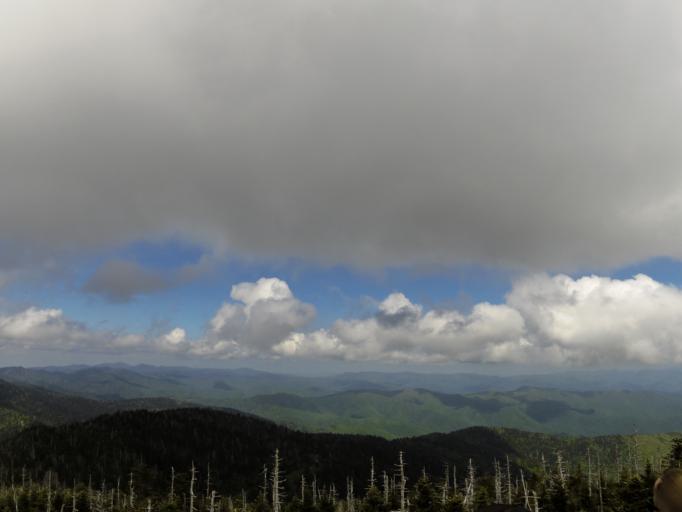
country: US
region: North Carolina
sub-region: Swain County
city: Bryson City
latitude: 35.5629
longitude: -83.4984
